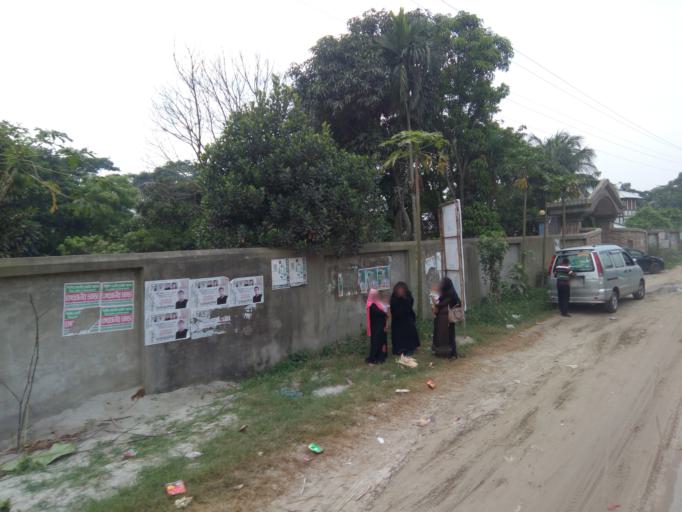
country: BD
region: Dhaka
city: Char Bhadrasan
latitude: 23.4704
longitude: 90.2874
